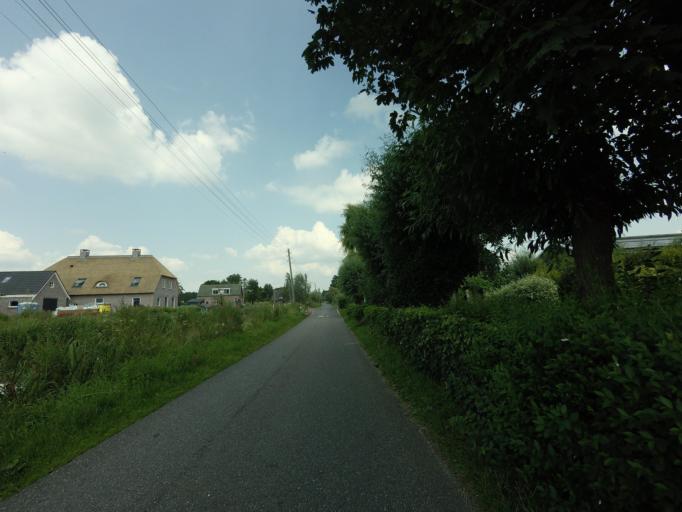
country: NL
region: South Holland
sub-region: Gemeente Gouda
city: Gouda
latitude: 51.9856
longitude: 4.7342
